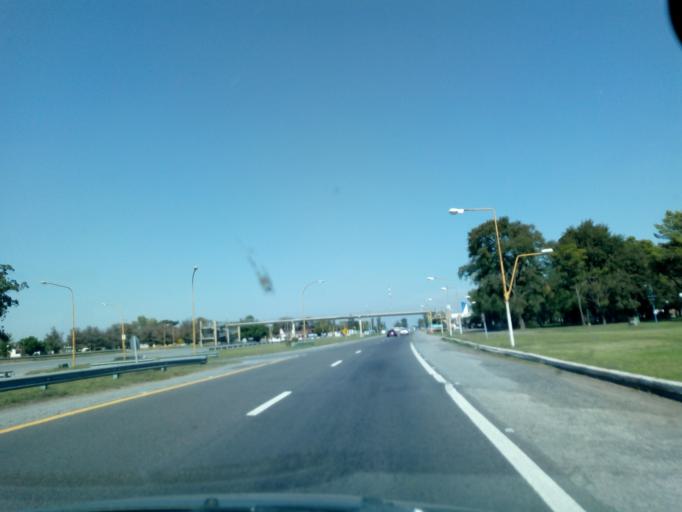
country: AR
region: Buenos Aires
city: Coronel Vidal
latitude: -37.2720
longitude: -57.7672
